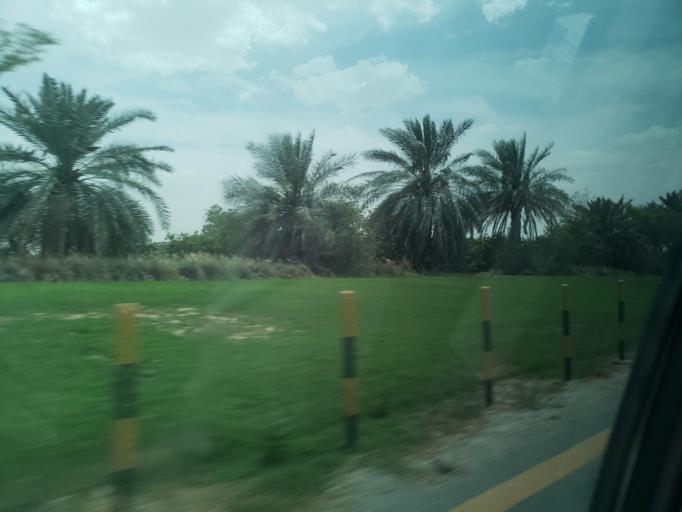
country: AE
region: Ash Shariqah
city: Sharjah
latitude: 25.3224
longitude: 55.5132
